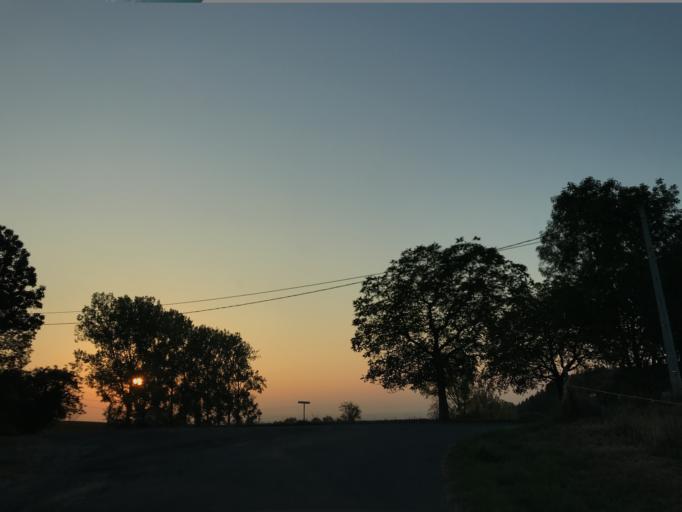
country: FR
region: Auvergne
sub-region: Departement du Puy-de-Dome
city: Escoutoux
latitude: 45.7663
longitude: 3.6277
